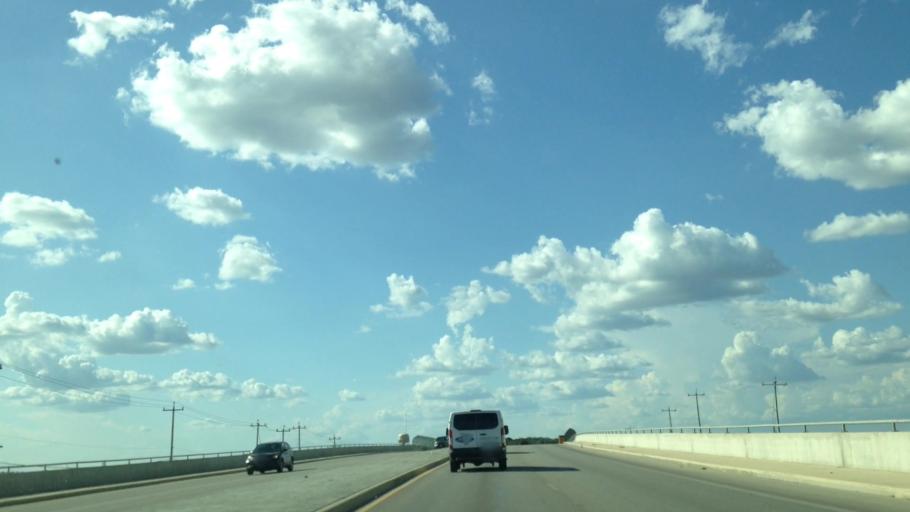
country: US
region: Texas
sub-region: Comal County
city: Garden Ridge
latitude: 29.6135
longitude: -98.2848
